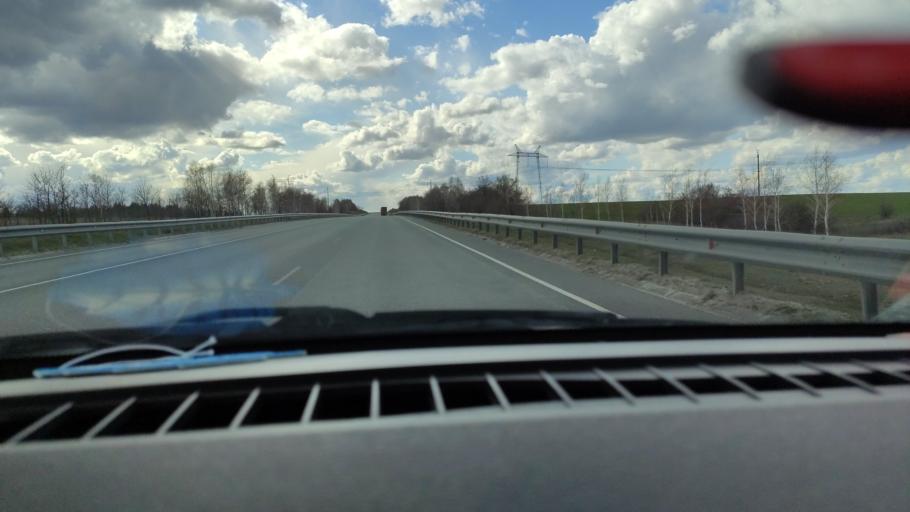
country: RU
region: Saratov
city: Tersa
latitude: 52.1010
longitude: 47.5099
